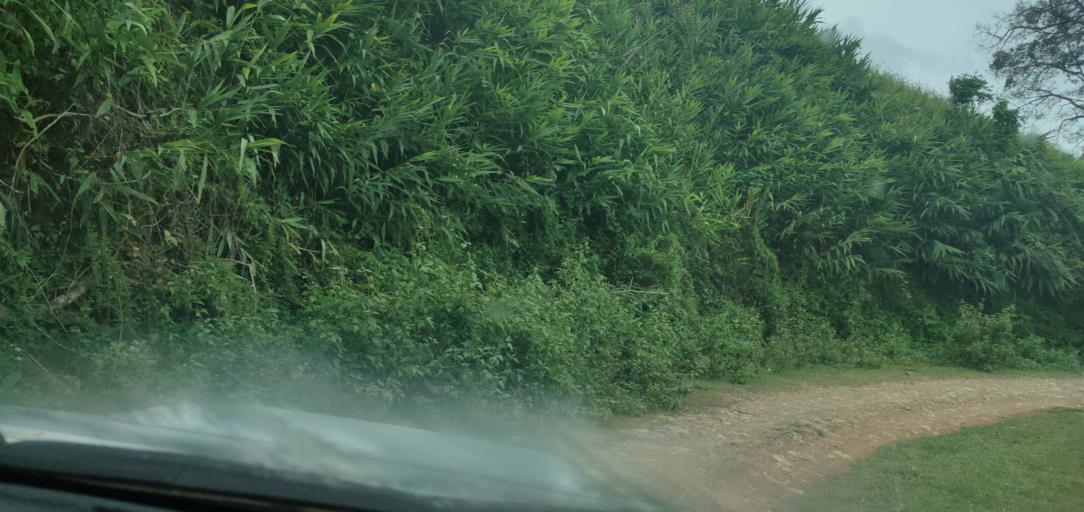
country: LA
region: Phongsali
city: Phongsali
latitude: 21.4415
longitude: 102.3199
